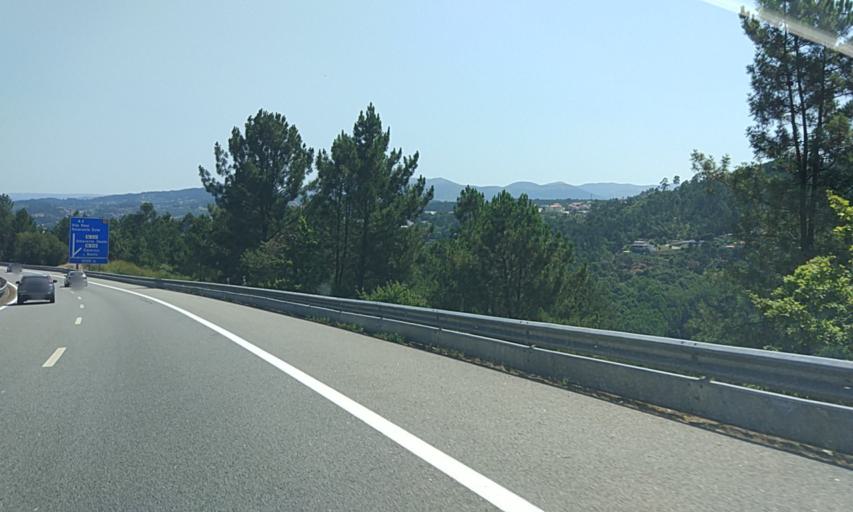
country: PT
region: Porto
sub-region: Amarante
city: Amarante
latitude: 41.2594
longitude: -8.1203
